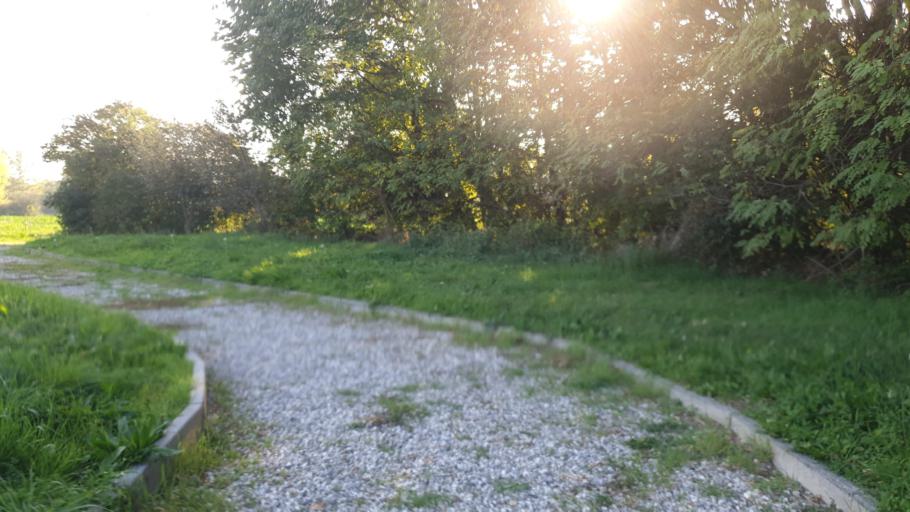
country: IT
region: Veneto
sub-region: Provincia di Padova
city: Ponte San Nicolo
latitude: 45.3795
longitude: 11.9433
